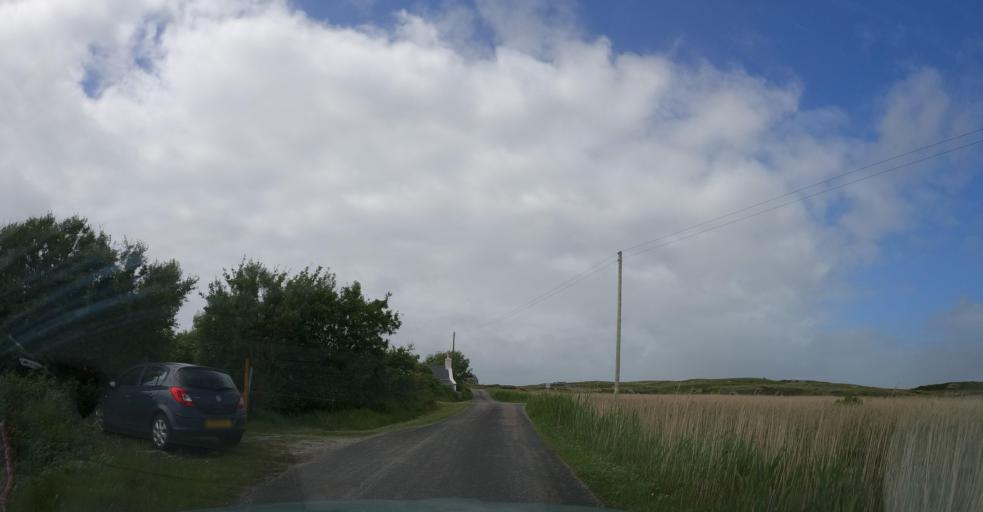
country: GB
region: Scotland
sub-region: Eilean Siar
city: Isle of South Uist
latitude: 57.2398
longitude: -7.3890
